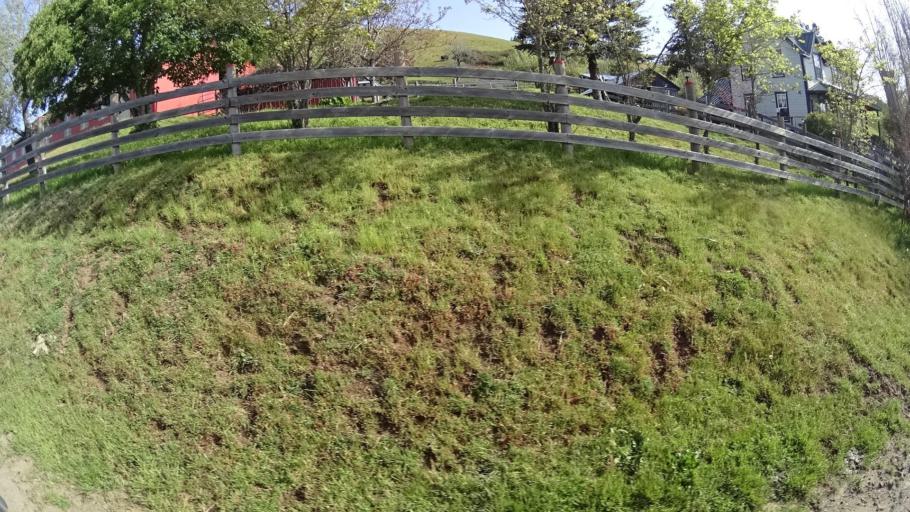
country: US
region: California
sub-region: Humboldt County
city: Hydesville
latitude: 40.6423
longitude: -123.9154
